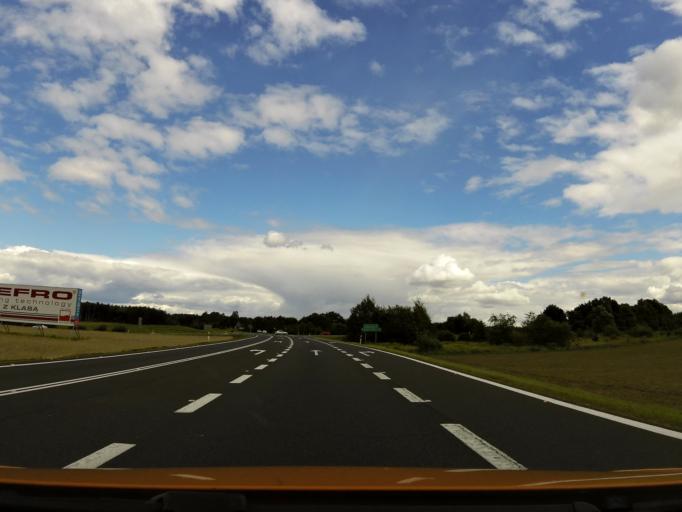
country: PL
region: West Pomeranian Voivodeship
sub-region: Powiat goleniowski
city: Goleniow
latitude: 53.5888
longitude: 14.8645
